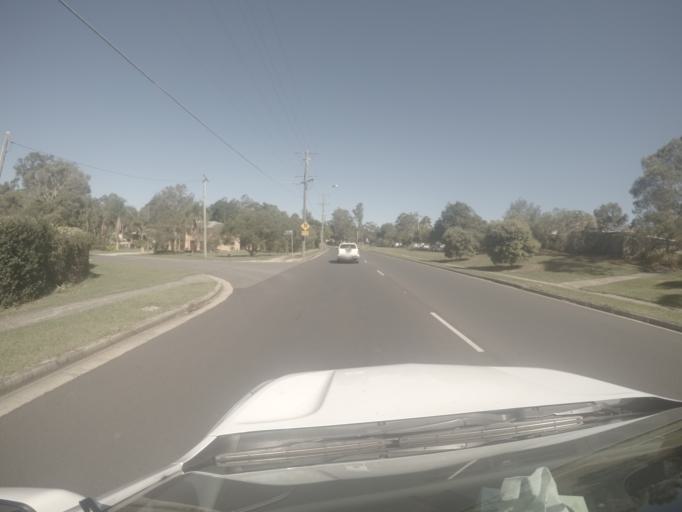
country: AU
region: Queensland
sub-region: Ipswich
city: Springfield
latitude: -27.6402
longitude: 152.9174
